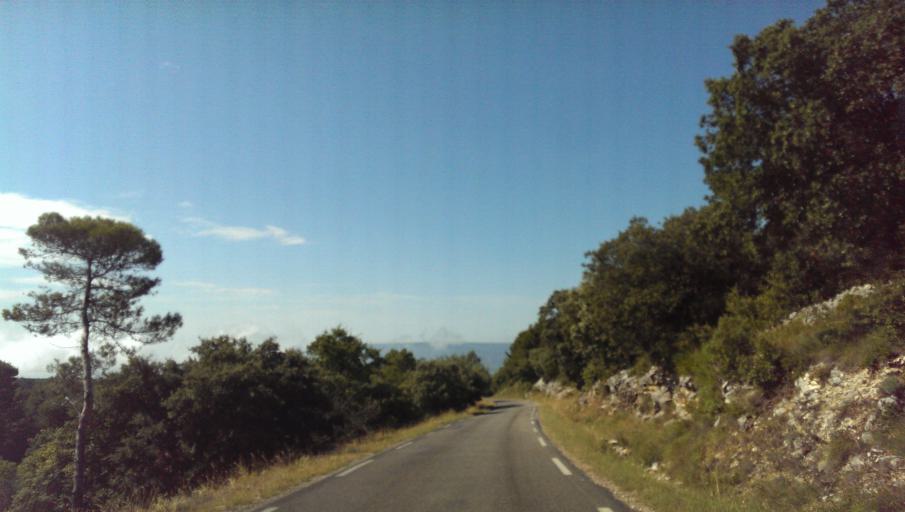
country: FR
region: Provence-Alpes-Cote d'Azur
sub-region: Departement du Vaucluse
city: Gordes
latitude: 43.9488
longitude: 5.1957
